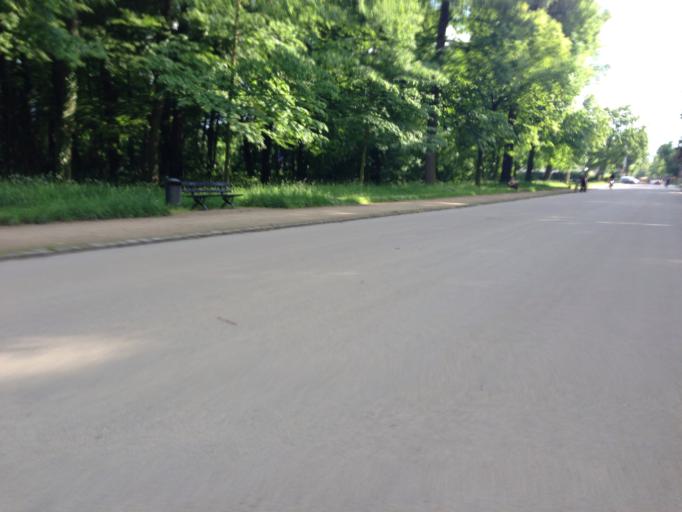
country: DE
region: Saxony
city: Dresden
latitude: 51.0354
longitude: 13.7604
